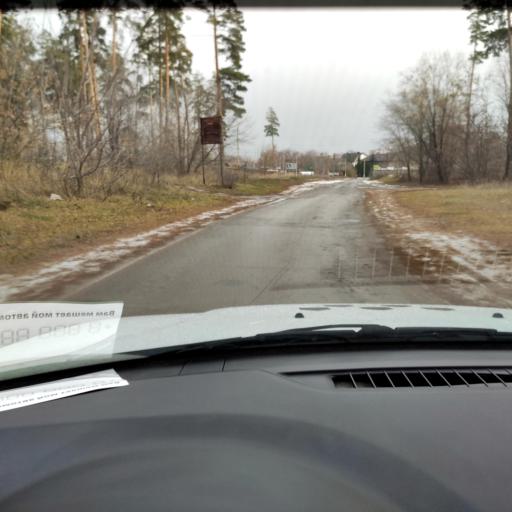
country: RU
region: Samara
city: Tol'yatti
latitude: 53.5081
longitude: 49.3878
